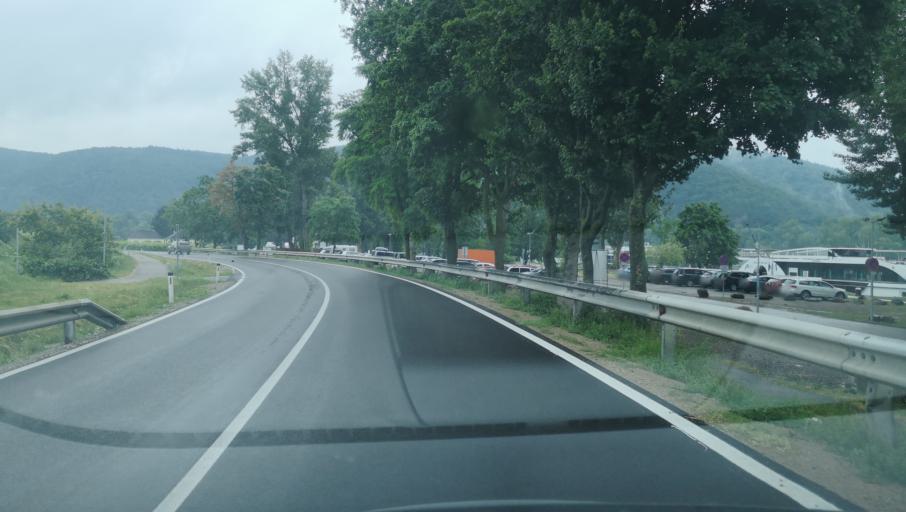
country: AT
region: Lower Austria
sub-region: Politischer Bezirk Krems
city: Durnstein
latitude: 48.3902
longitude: 15.5227
